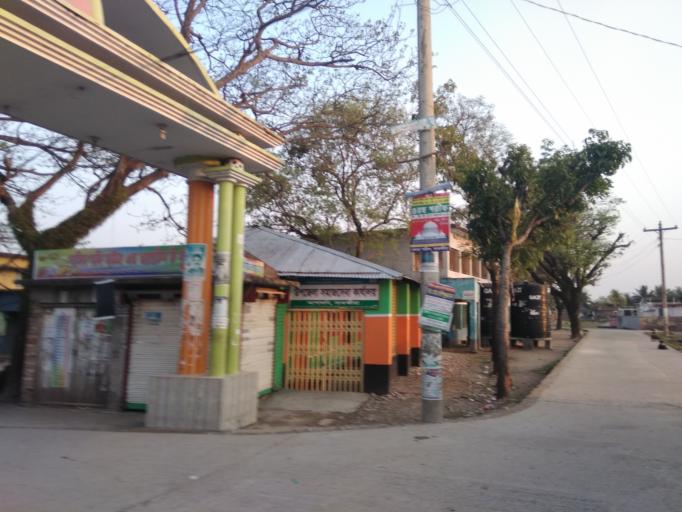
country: BD
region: Khulna
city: Satkhira
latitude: 22.5478
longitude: 89.1774
